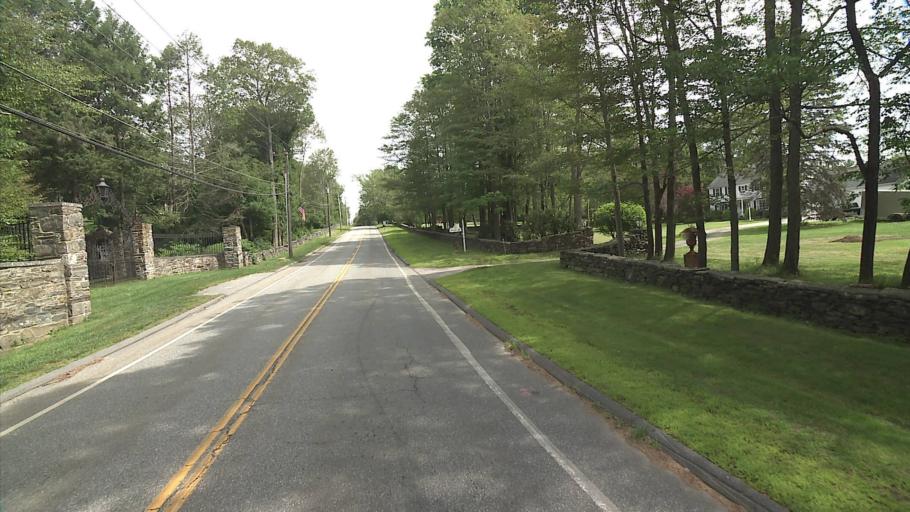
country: US
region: Connecticut
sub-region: Windham County
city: Thompson
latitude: 41.9542
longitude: -71.8660
